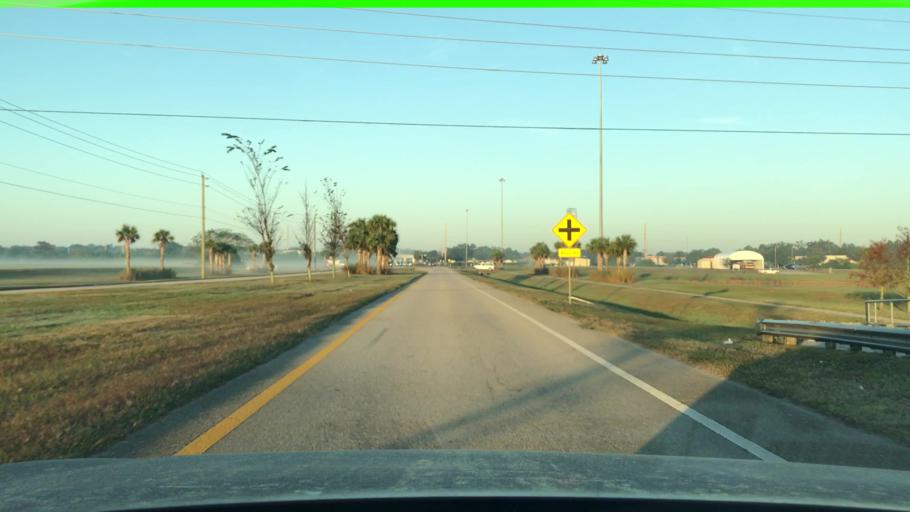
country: US
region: Florida
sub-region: Sarasota County
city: Fruitville
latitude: 27.3257
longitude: -82.4411
